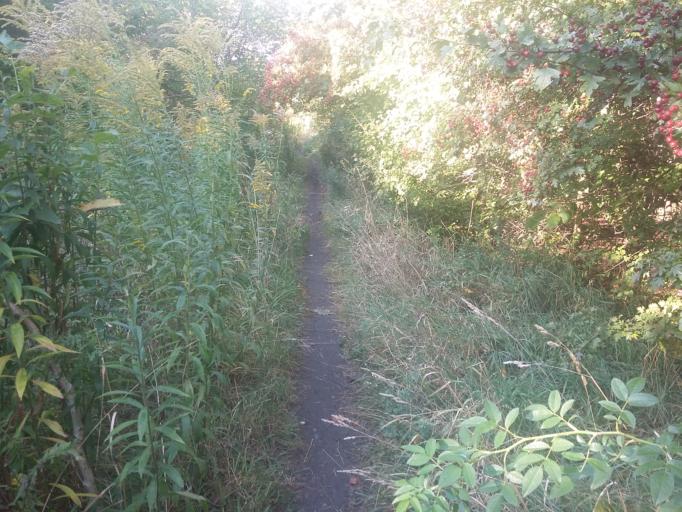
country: PL
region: Lodz Voivodeship
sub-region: Powiat pabianicki
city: Ksawerow
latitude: 51.7383
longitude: 19.4003
